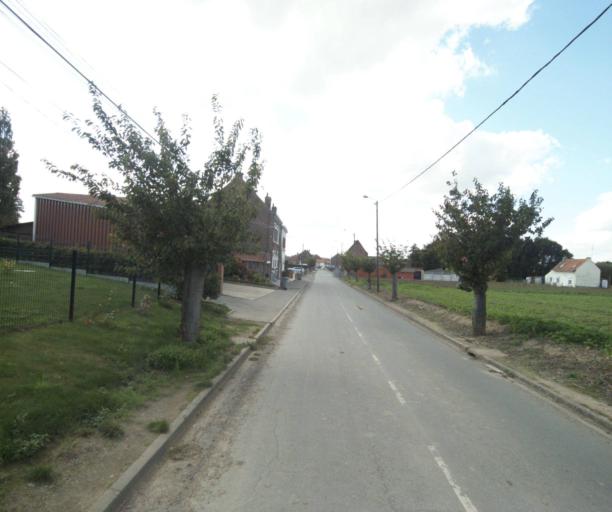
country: FR
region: Nord-Pas-de-Calais
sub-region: Departement du Nord
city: Illies
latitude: 50.5558
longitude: 2.8231
